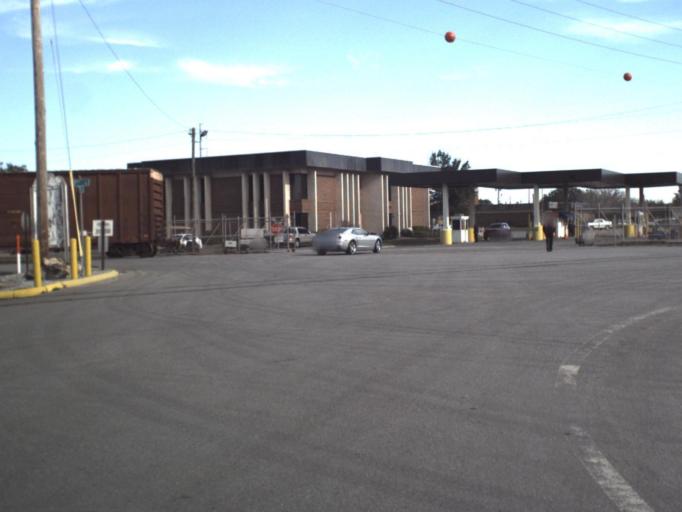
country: US
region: Florida
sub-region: Bay County
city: Upper Grand Lagoon
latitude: 30.1823
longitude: -85.7304
